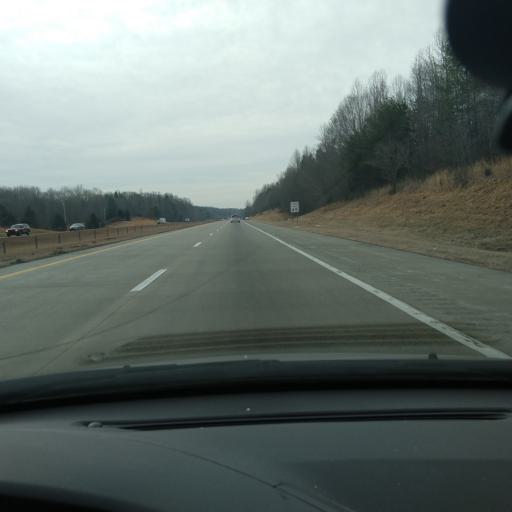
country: US
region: North Carolina
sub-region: Davidson County
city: Welcome
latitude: 35.8963
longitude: -80.2332
